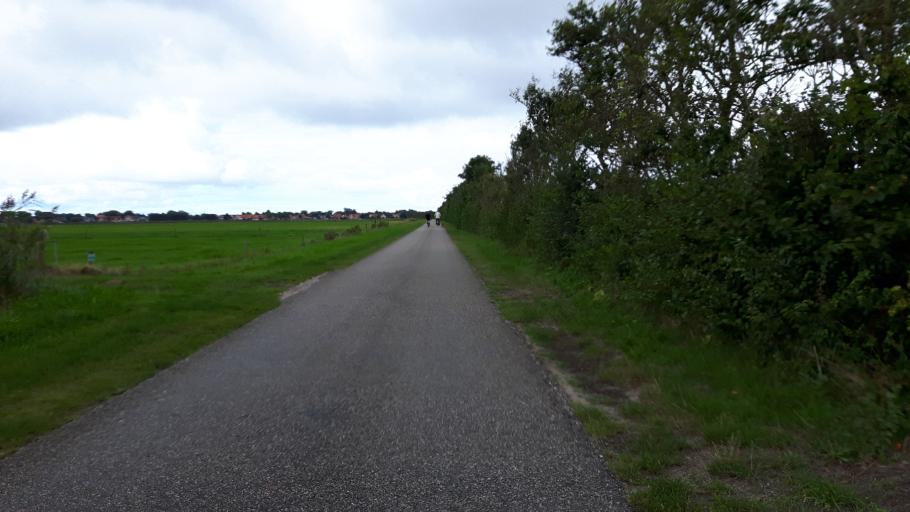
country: NL
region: Friesland
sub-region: Gemeente Ameland
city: Hollum
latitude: 53.4415
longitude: 5.6603
